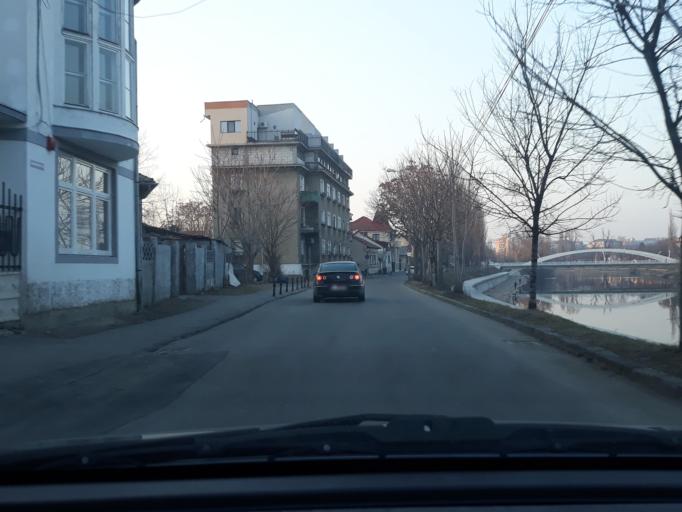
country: RO
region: Bihor
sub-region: Comuna Biharea
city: Oradea
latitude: 47.0582
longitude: 21.9264
